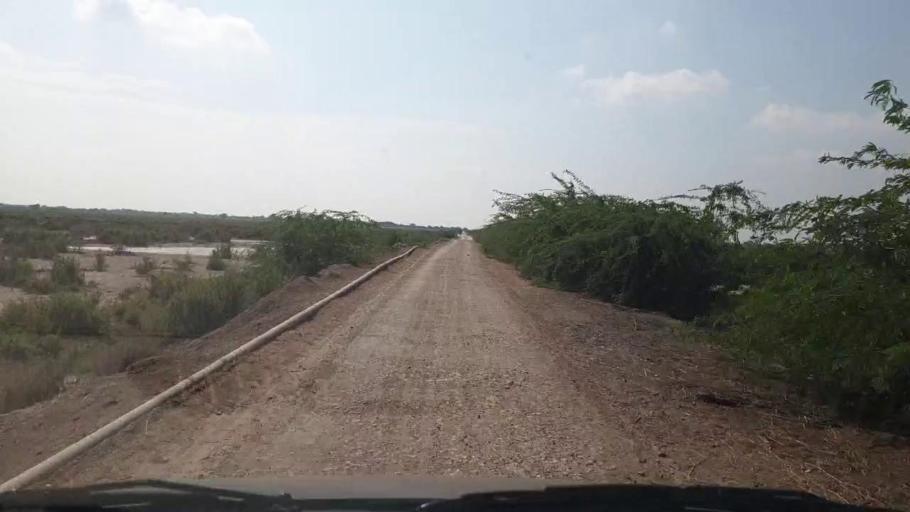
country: PK
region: Sindh
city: Badin
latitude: 24.4989
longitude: 68.6066
